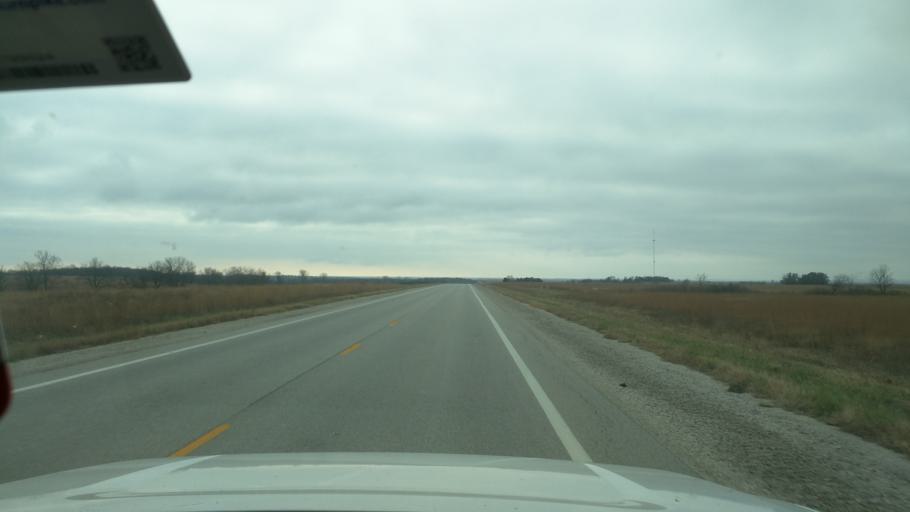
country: US
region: Kansas
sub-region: Elk County
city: Howard
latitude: 37.5603
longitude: -96.2532
